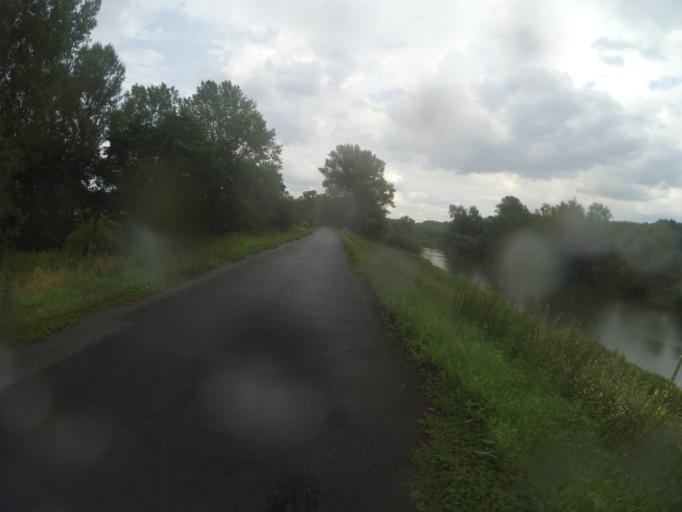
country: CZ
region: Central Bohemia
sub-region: Okres Melnik
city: Melnik
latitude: 50.3233
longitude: 14.4639
